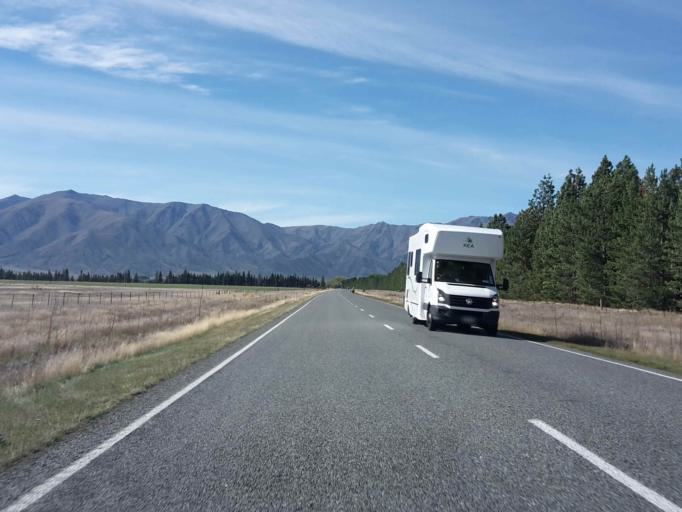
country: NZ
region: Otago
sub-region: Queenstown-Lakes District
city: Wanaka
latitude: -44.4931
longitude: 169.9325
